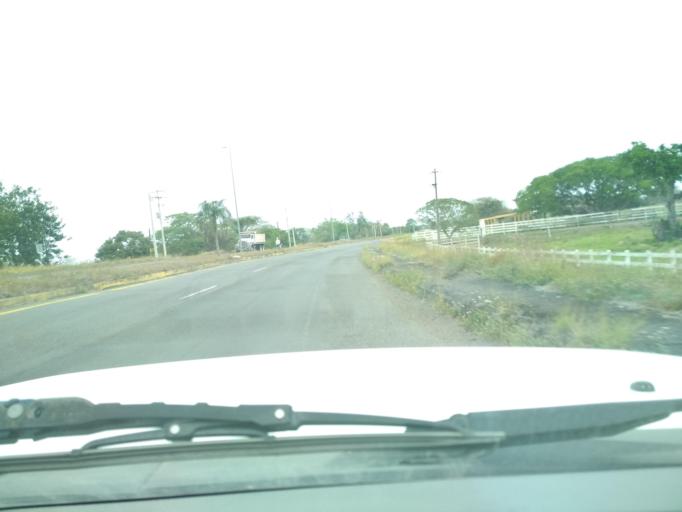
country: MX
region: Veracruz
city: El Tejar
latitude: 19.0684
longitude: -96.1310
